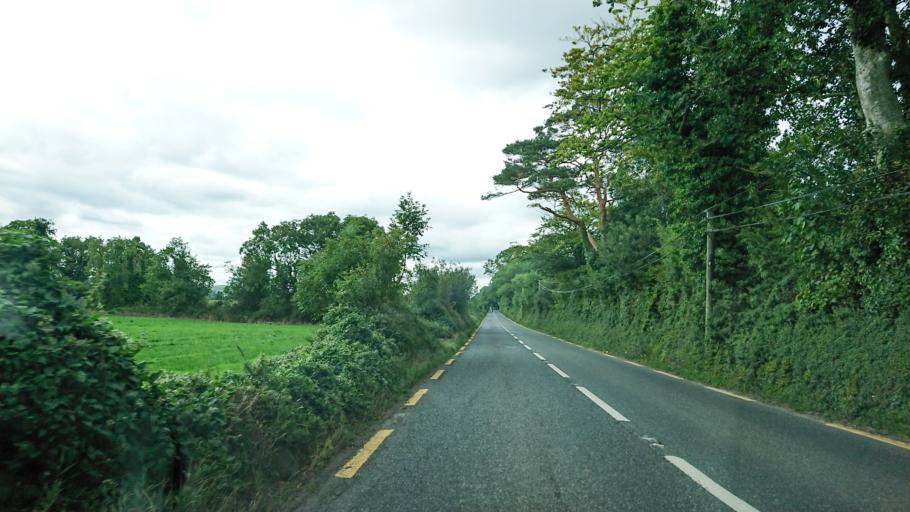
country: IE
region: Munster
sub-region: Waterford
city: Dungarvan
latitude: 52.1115
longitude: -7.6083
